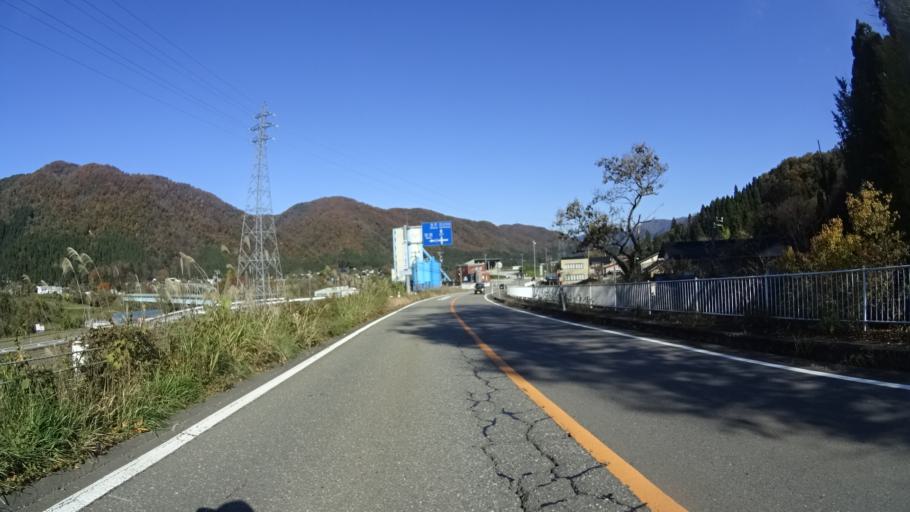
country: JP
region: Ishikawa
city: Tsurugi-asahimachi
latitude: 36.3856
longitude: 136.6124
